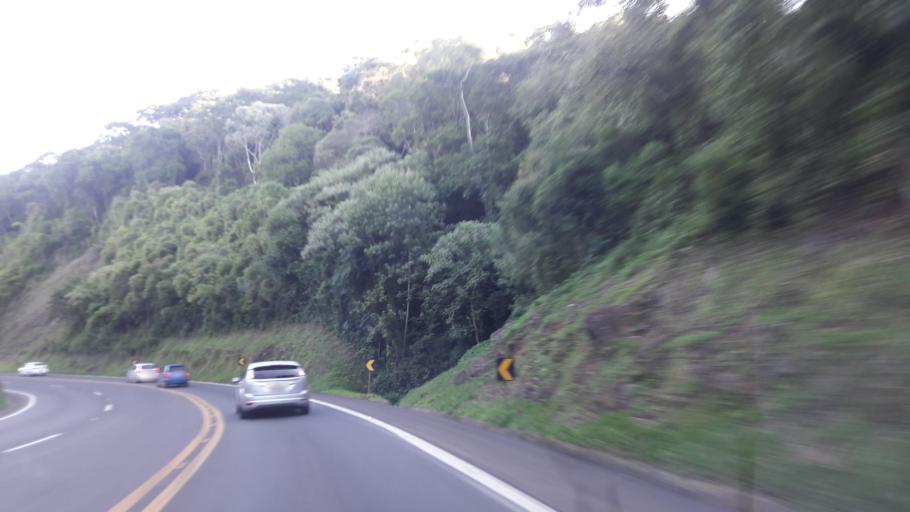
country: BR
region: Parana
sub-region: Prudentopolis
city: Prudentopolis
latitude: -25.3097
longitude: -51.2087
